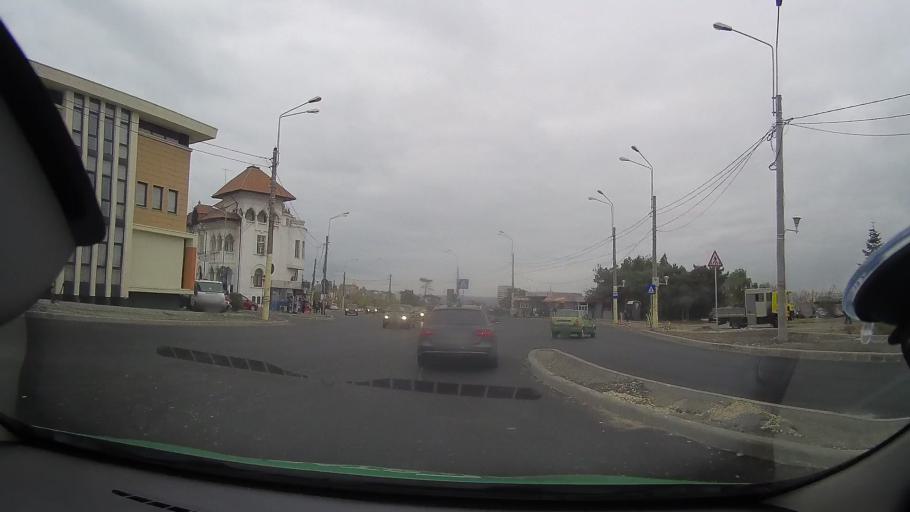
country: RO
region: Constanta
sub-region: Municipiul Constanta
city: Constanta
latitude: 44.1756
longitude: 28.6515
